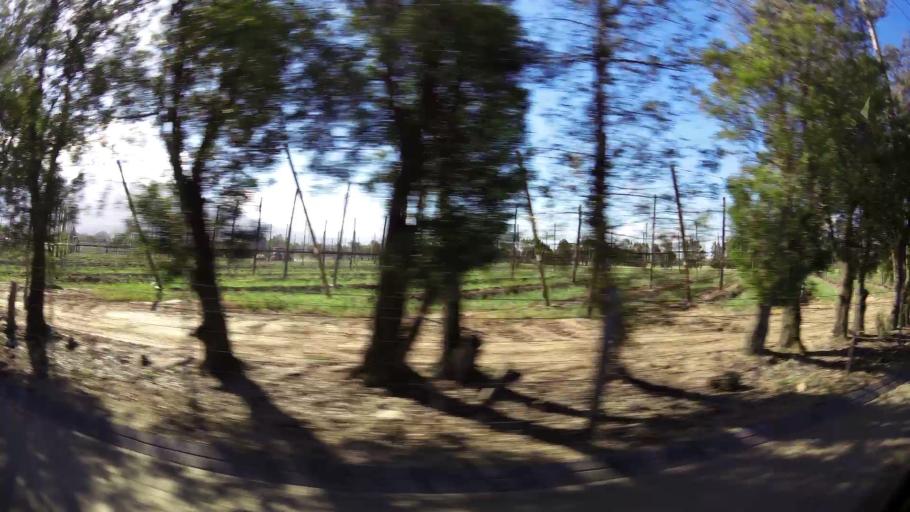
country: ZA
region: Western Cape
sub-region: Eden District Municipality
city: George
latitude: -33.9612
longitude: 22.3993
